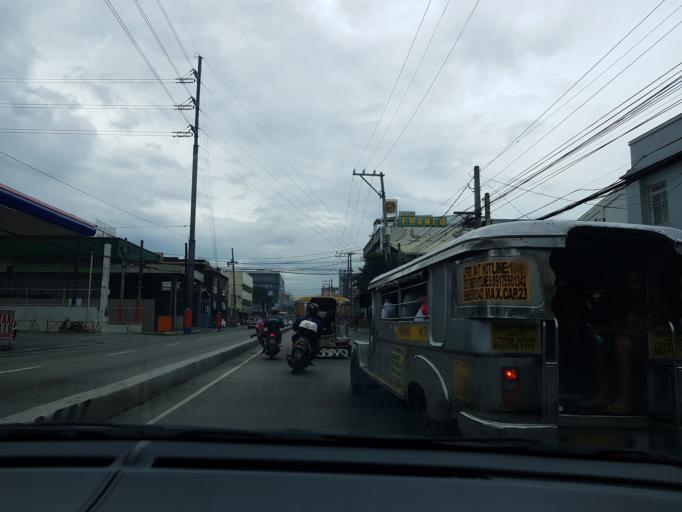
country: PH
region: Metro Manila
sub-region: Caloocan City
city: Niugan
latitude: 14.6627
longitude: 120.9841
